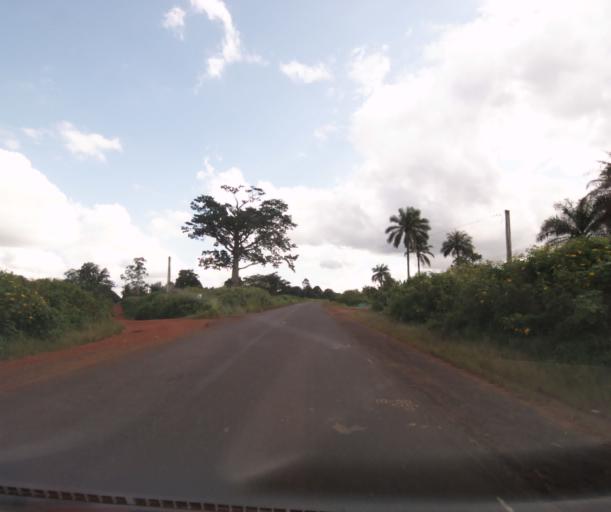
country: CM
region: West
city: Foumban
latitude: 5.6940
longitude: 10.8110
